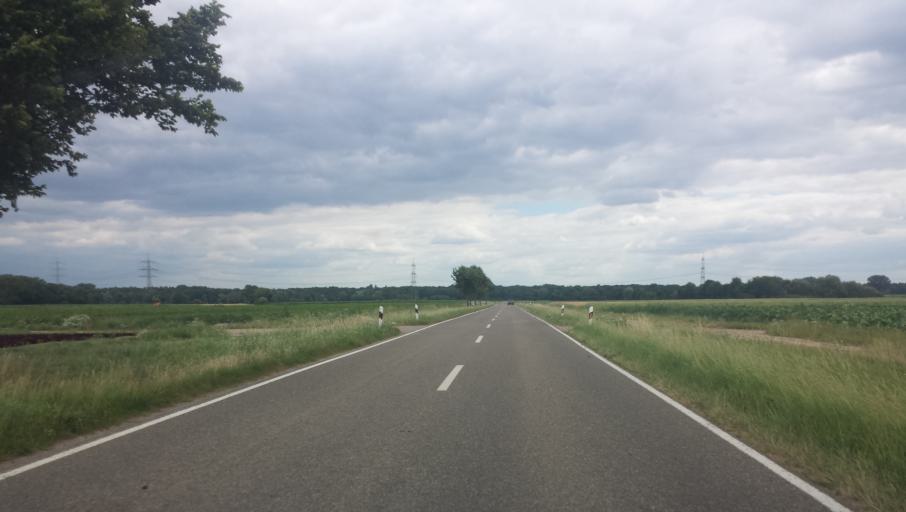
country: DE
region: Rheinland-Pfalz
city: Gommersheim
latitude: 49.2921
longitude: 8.2838
